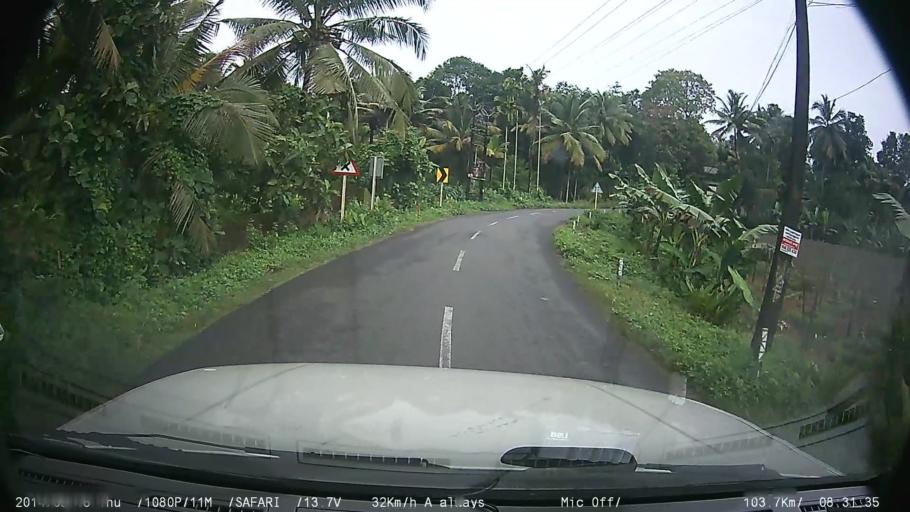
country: IN
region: Kerala
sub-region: Kottayam
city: Palackattumala
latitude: 9.7014
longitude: 76.6098
